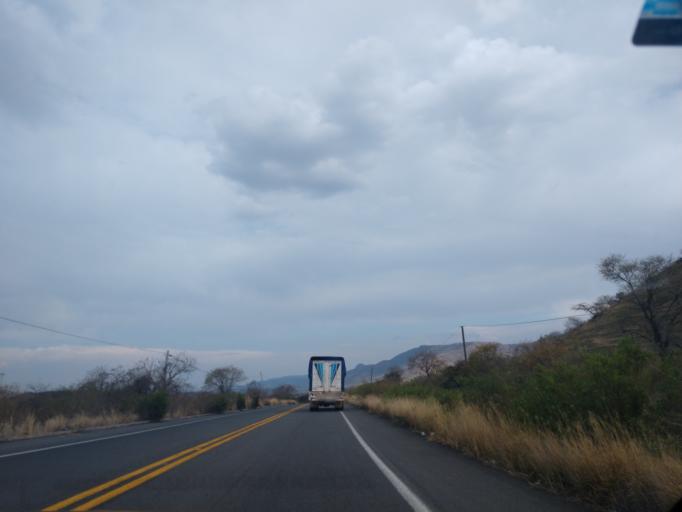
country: MX
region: Jalisco
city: La Manzanilla de la Paz
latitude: 20.1210
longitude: -103.1616
